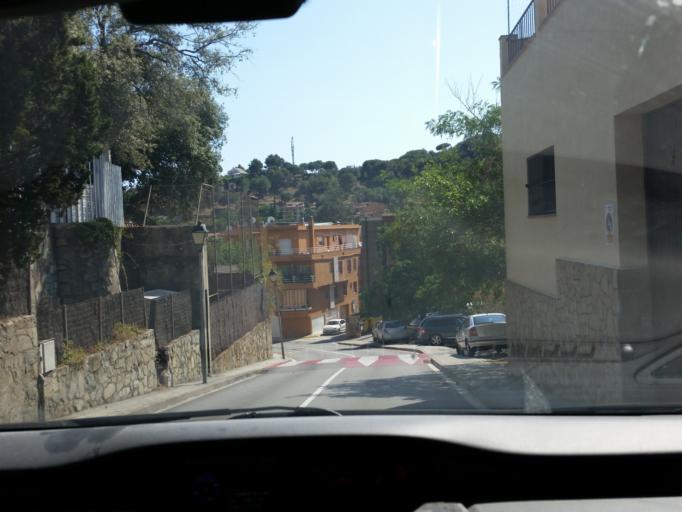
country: ES
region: Catalonia
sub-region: Provincia de Barcelona
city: Cabrils
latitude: 41.5278
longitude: 2.3655
